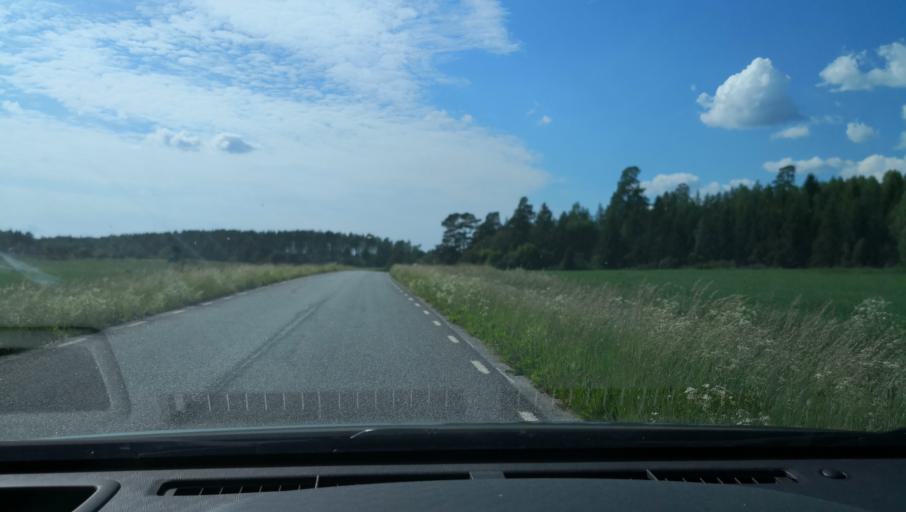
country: SE
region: Uppsala
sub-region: Enkopings Kommun
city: Orsundsbro
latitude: 59.8393
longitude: 17.2947
